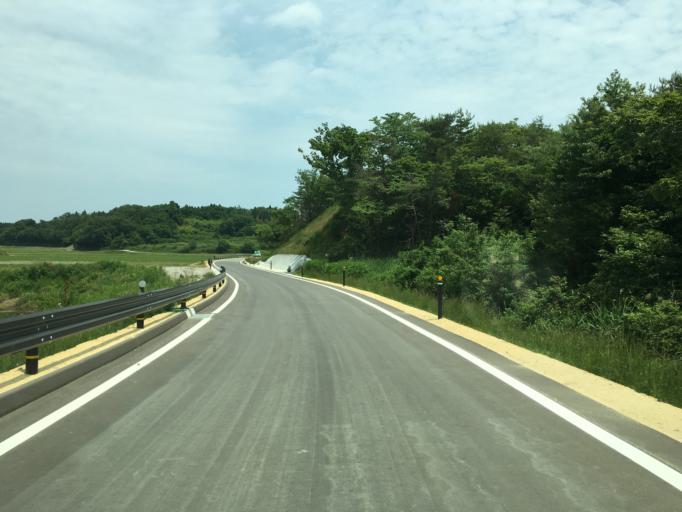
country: JP
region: Miyagi
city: Marumori
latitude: 37.7579
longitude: 140.9822
